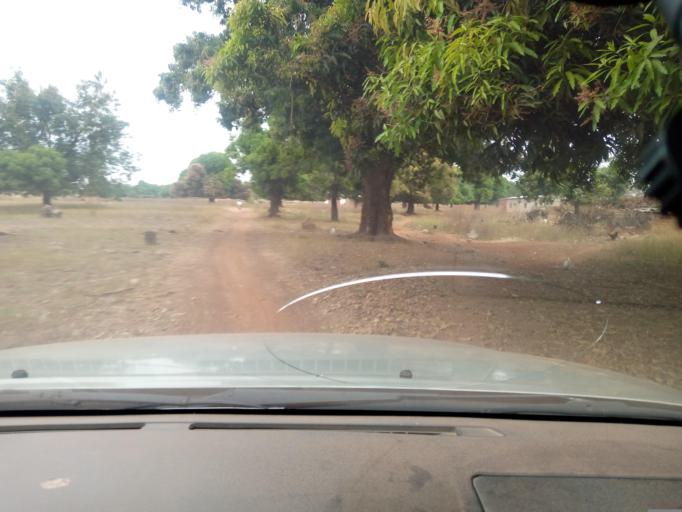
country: ML
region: Sikasso
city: Sikasso
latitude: 10.9707
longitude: -5.6926
